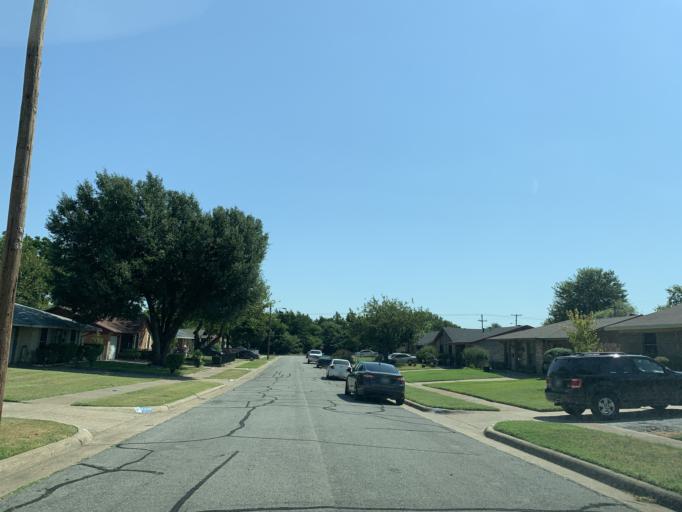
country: US
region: Texas
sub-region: Dallas County
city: Hutchins
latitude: 32.6688
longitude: -96.7461
